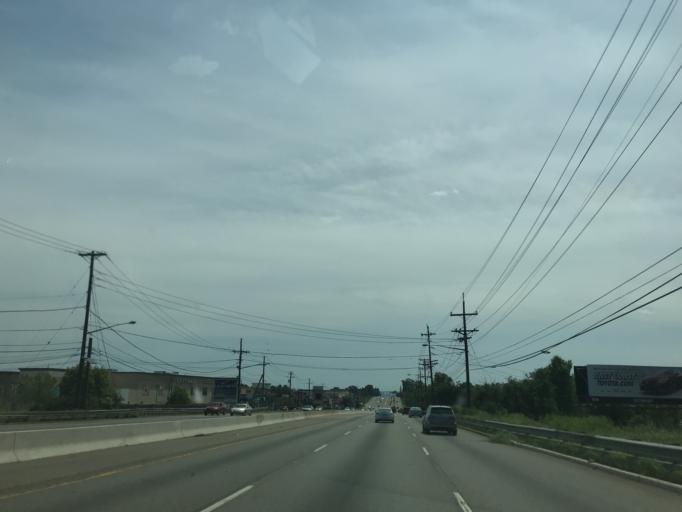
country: US
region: New Jersey
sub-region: Essex County
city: Nutley
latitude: 40.8392
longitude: -74.1588
